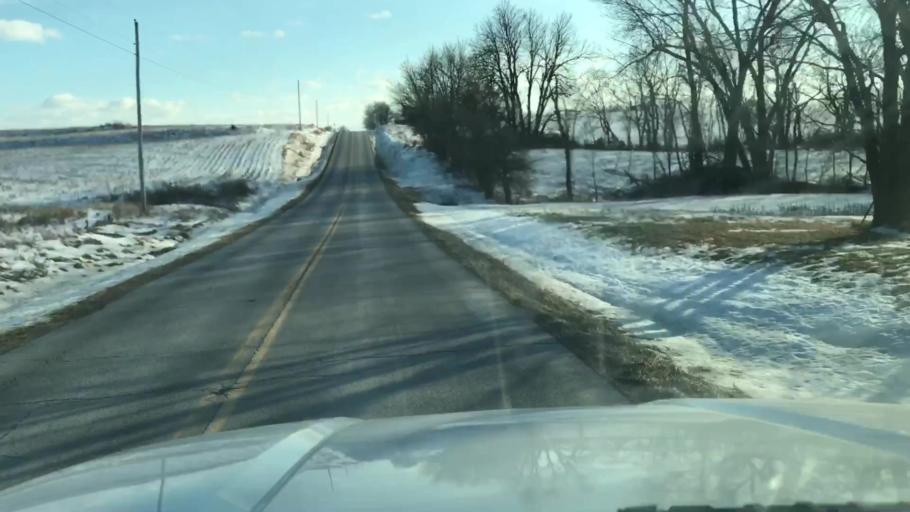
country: US
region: Missouri
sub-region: Holt County
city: Oregon
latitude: 40.0545
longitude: -94.9749
